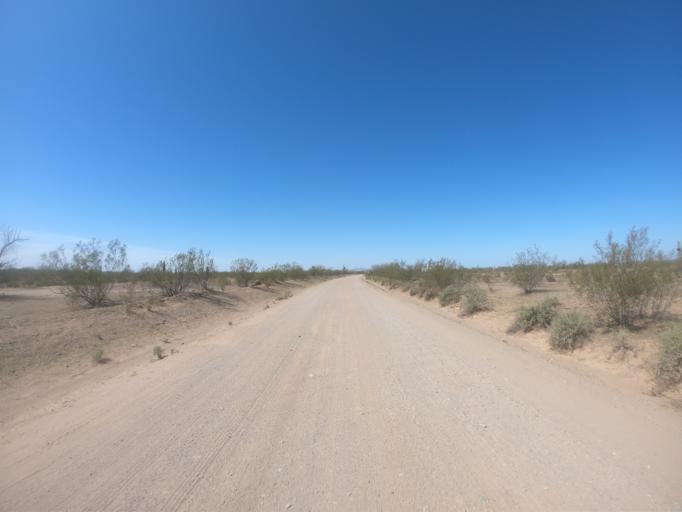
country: US
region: Arizona
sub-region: Pinal County
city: Gold Camp
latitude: 33.2397
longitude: -111.3351
